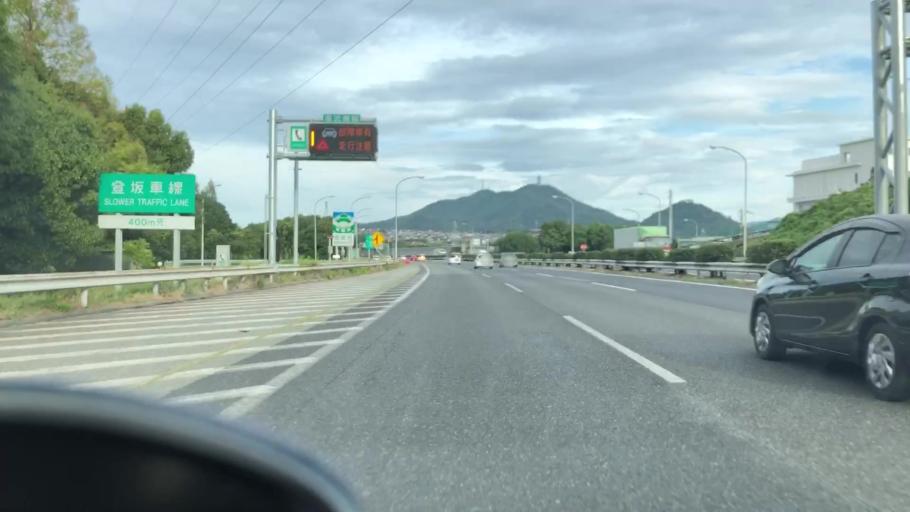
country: JP
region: Hyogo
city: Sandacho
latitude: 34.8390
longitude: 135.2335
